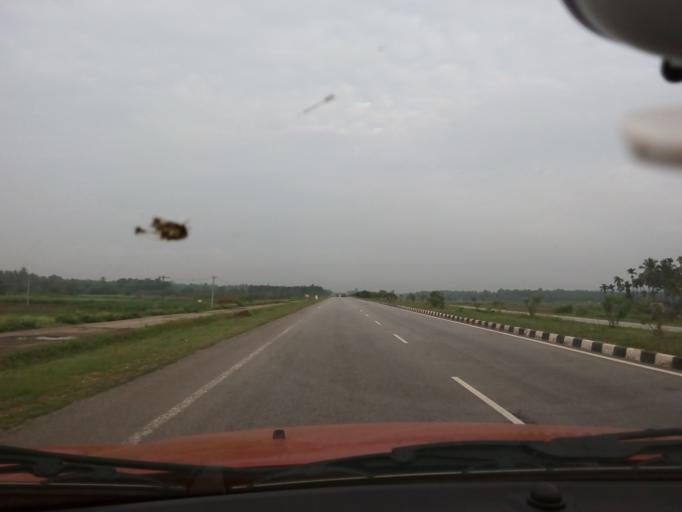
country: IN
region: Karnataka
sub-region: Tumkur
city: Kunigal
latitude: 13.0050
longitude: 77.0028
